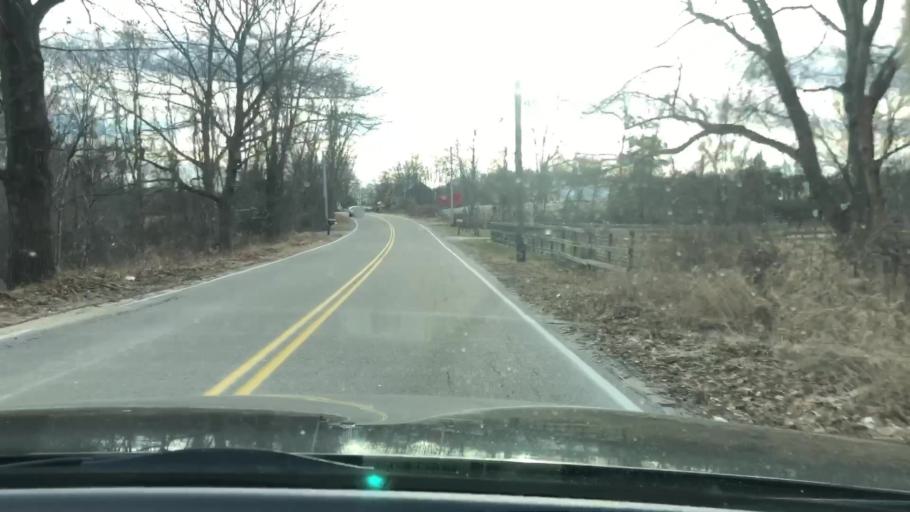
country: US
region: Massachusetts
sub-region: Worcester County
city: Blackstone
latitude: 42.0569
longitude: -71.5296
